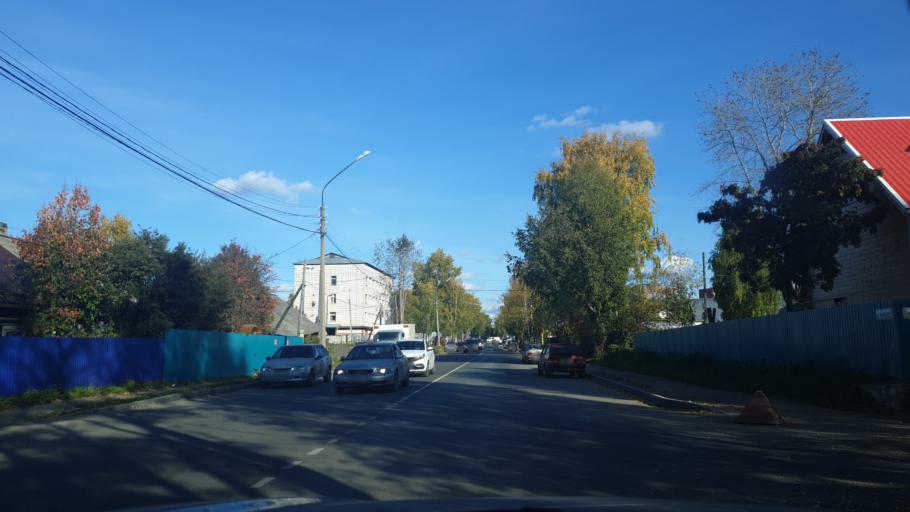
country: RU
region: Komi Republic
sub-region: Syktyvdinskiy Rayon
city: Syktyvkar
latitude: 61.6849
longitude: 50.8033
